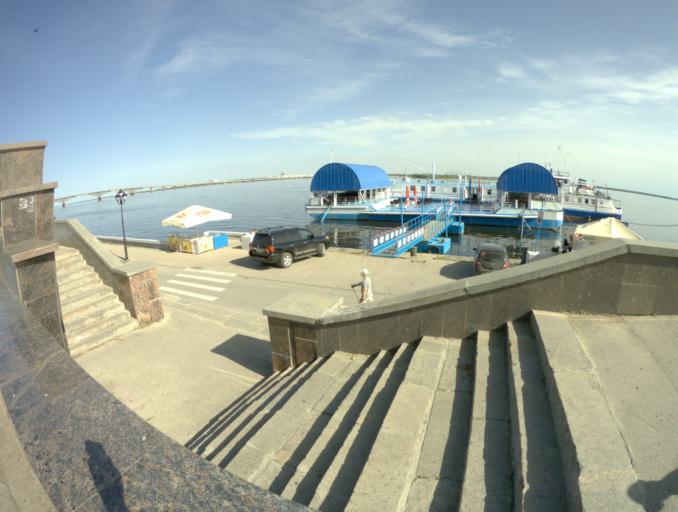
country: RU
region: Saratov
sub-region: Saratovskiy Rayon
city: Saratov
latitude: 51.5247
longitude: 46.0474
